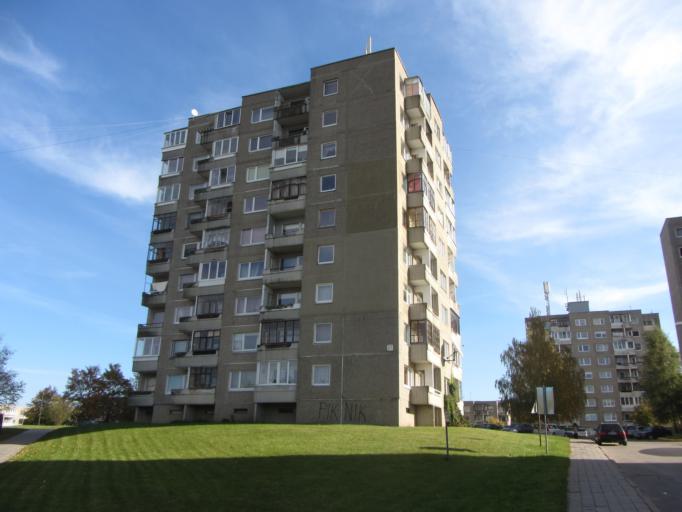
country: LT
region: Vilnius County
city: Elektrenai
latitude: 54.7857
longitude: 24.6774
